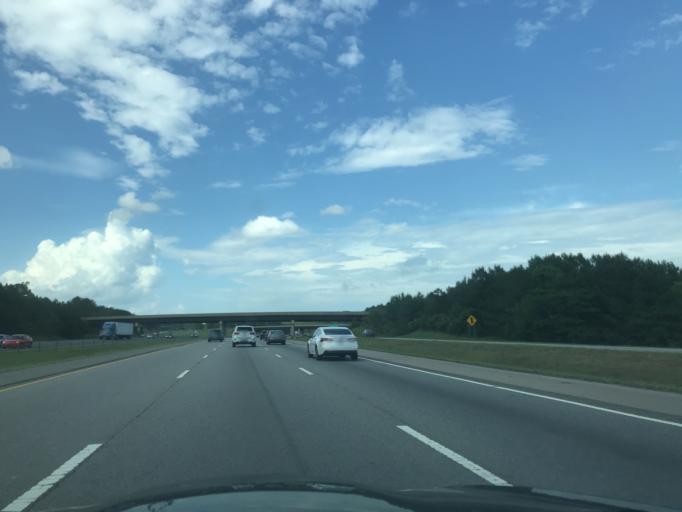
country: US
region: North Carolina
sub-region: Wake County
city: Morrisville
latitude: 35.8883
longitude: -78.8177
